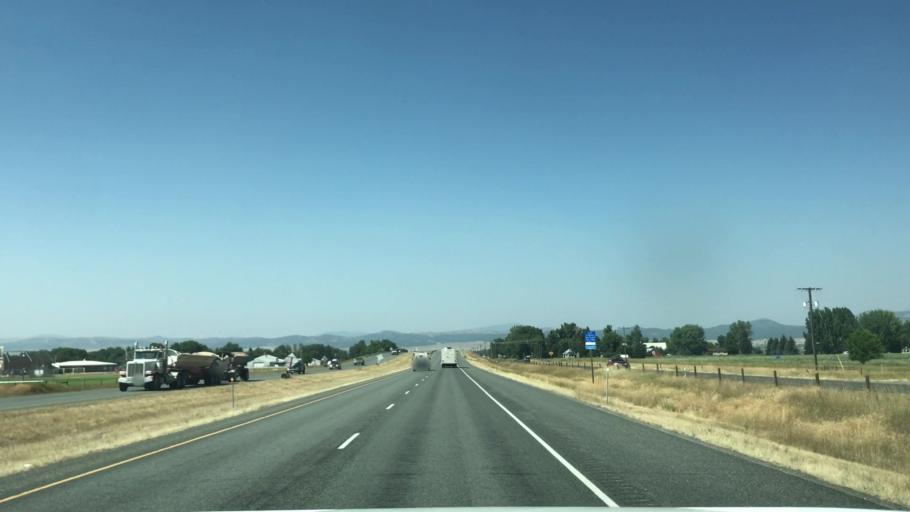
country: US
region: Montana
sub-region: Lewis and Clark County
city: Helena Valley West Central
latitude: 46.6559
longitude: -112.0116
